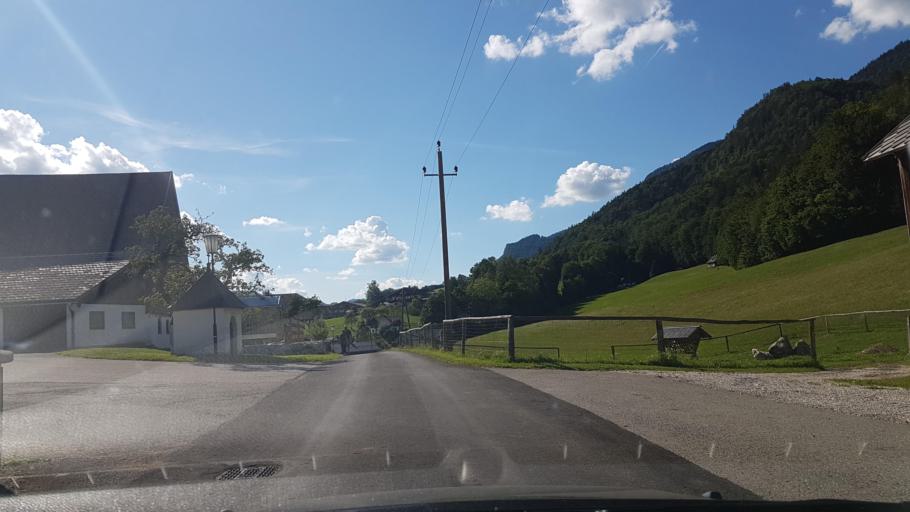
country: AT
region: Upper Austria
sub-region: Politischer Bezirk Gmunden
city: Sankt Wolfgang im Salzkammergut
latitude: 47.7365
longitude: 13.4630
